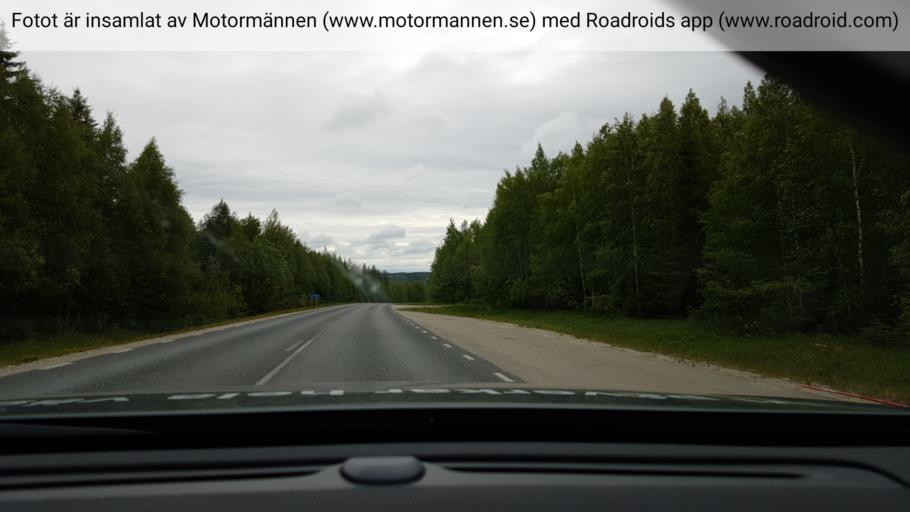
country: SE
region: Vaesterbotten
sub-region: Lycksele Kommun
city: Lycksele
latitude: 64.5069
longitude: 18.3135
